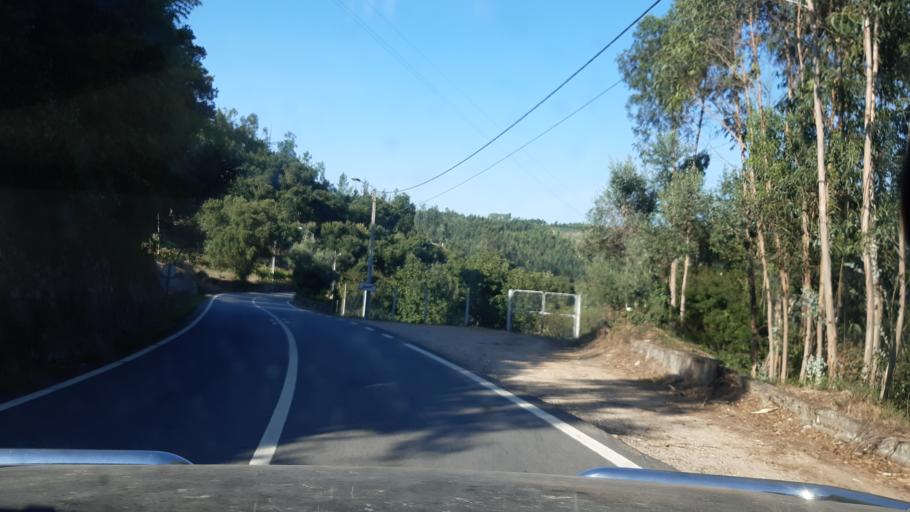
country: PT
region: Aveiro
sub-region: Agueda
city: Agueda
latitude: 40.5642
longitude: -8.4074
